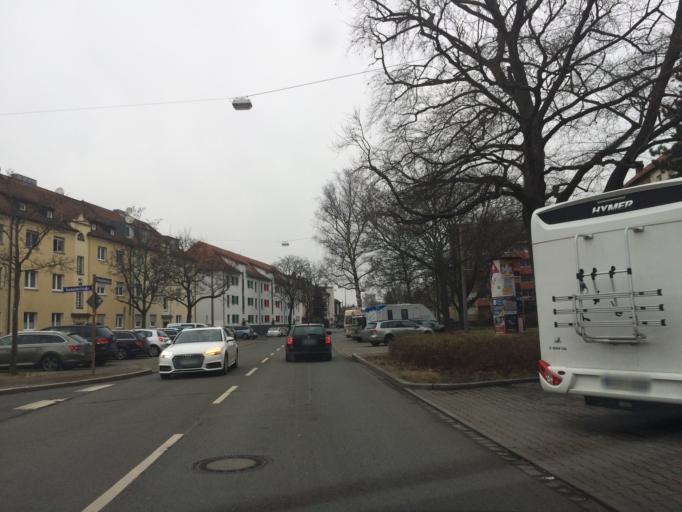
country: DE
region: Bavaria
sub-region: Regierungsbezirk Mittelfranken
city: Nuernberg
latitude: 49.4688
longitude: 11.0890
